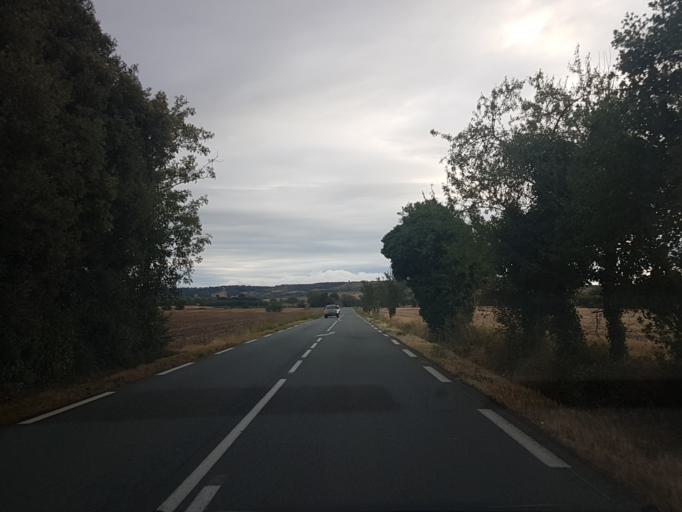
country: FR
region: Languedoc-Roussillon
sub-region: Departement de l'Aude
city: Bram
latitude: 43.2099
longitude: 2.0680
